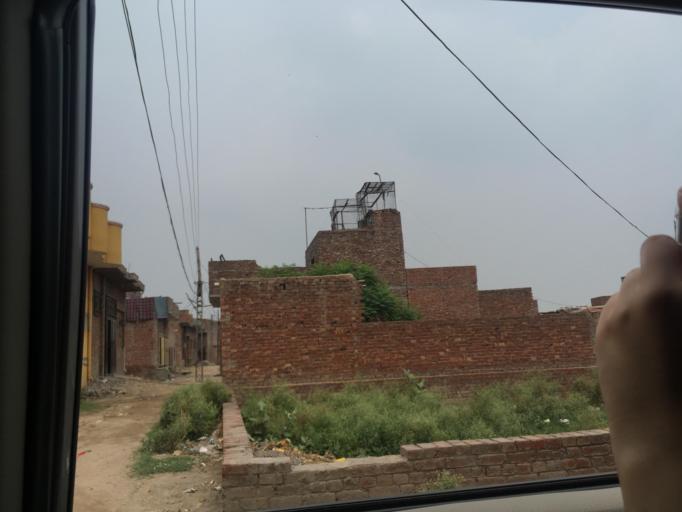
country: PK
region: Punjab
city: Lahore
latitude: 31.6171
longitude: 74.3551
